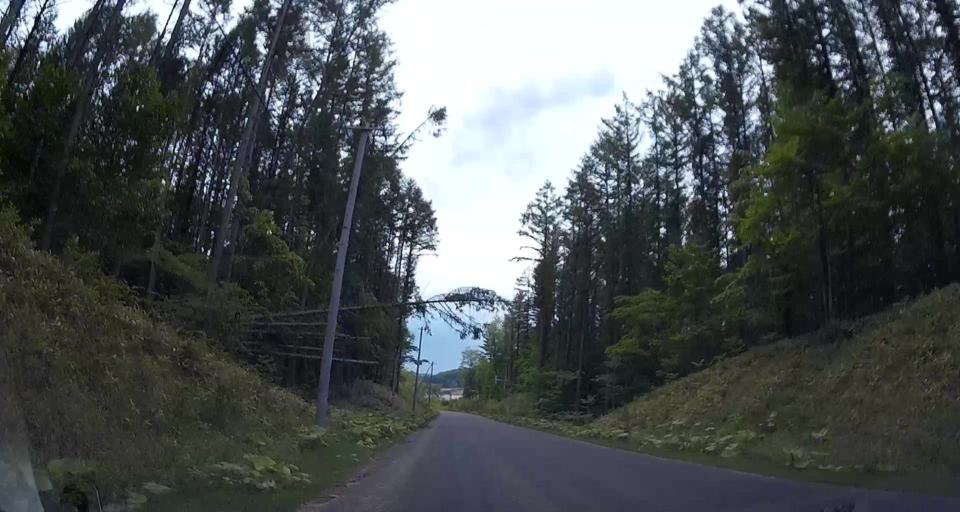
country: JP
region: Hokkaido
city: Chitose
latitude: 42.7795
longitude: 142.0131
